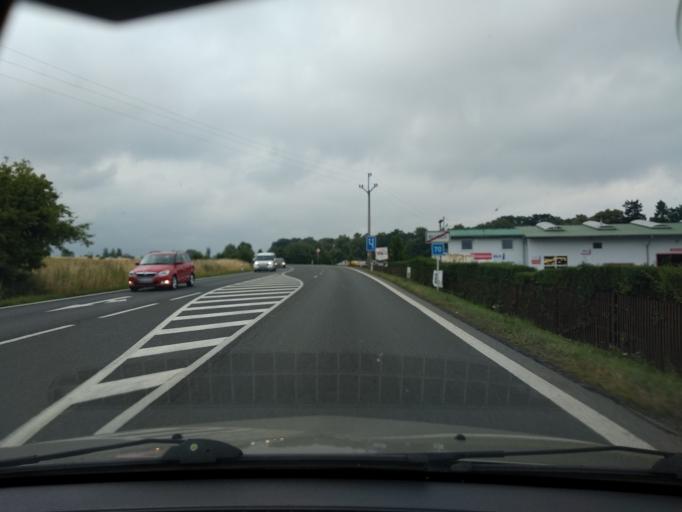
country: CZ
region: Olomoucky
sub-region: Okres Sumperk
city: Bludov
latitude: 49.9420
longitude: 16.9336
